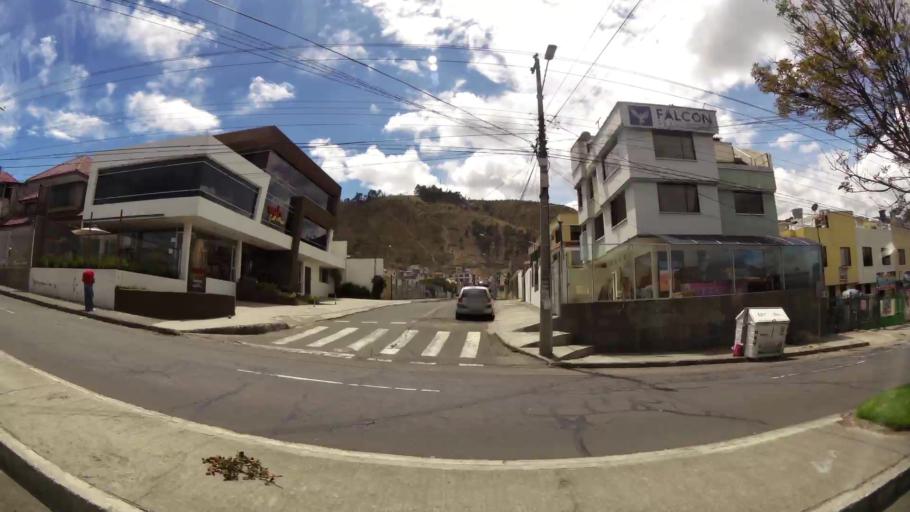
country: EC
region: Tungurahua
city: Ambato
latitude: -1.2618
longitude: -78.6394
